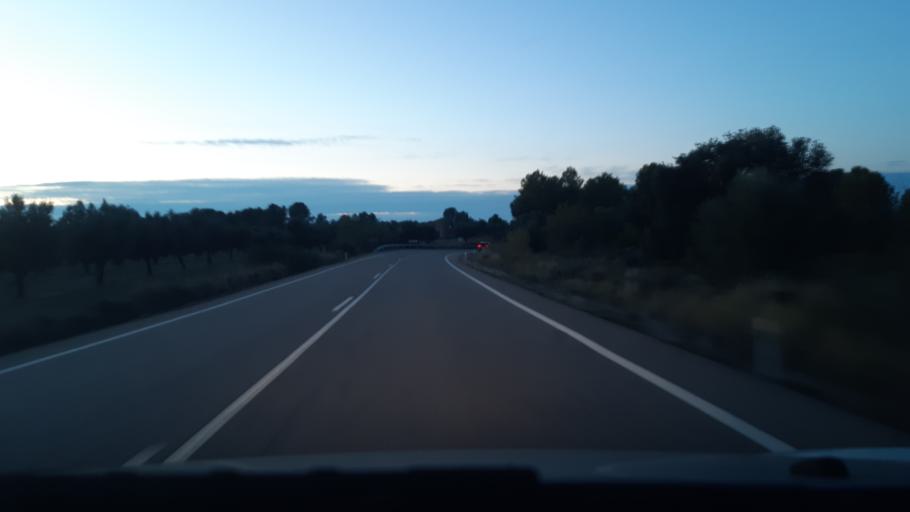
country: ES
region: Aragon
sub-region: Provincia de Teruel
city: Calaceite
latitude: 40.9635
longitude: 0.2096
